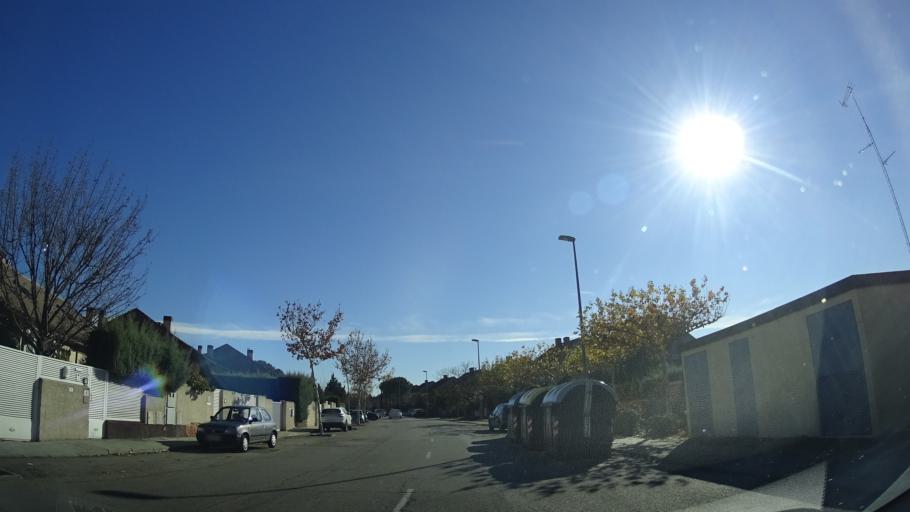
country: ES
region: Madrid
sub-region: Provincia de Madrid
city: Las Matas
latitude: 40.5226
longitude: -3.9122
